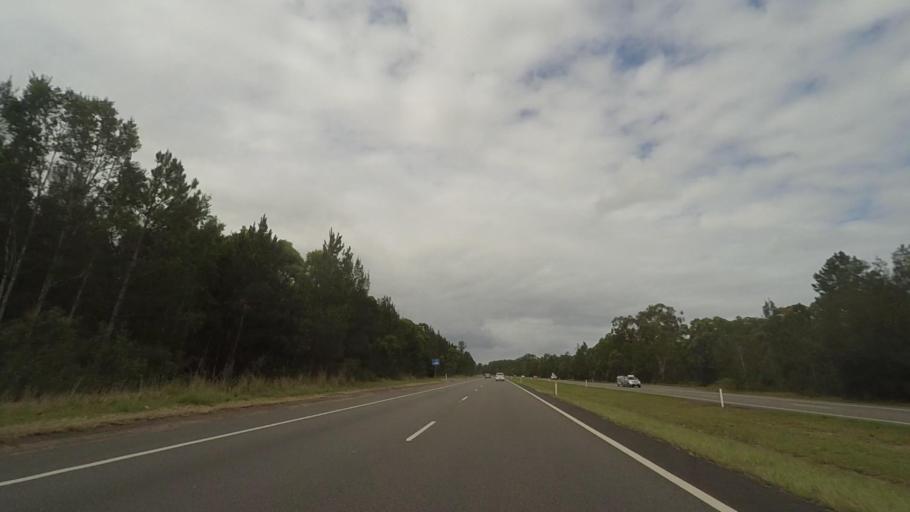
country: AU
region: New South Wales
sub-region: Port Stephens Shire
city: Raymond Terrace
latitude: -32.7736
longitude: 151.7580
